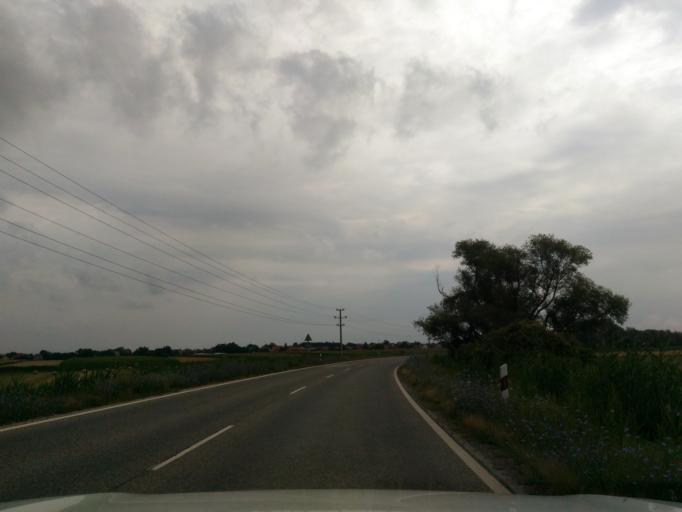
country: HU
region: Pest
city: Ujhartyan
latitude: 47.2141
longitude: 19.3765
